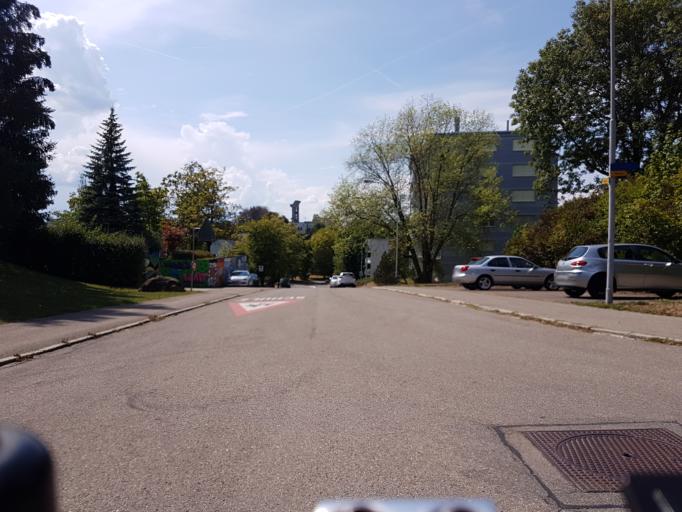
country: CH
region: Zurich
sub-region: Bezirk Pfaeffikon
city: Effretikon / Watt
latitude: 47.4294
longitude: 8.6949
